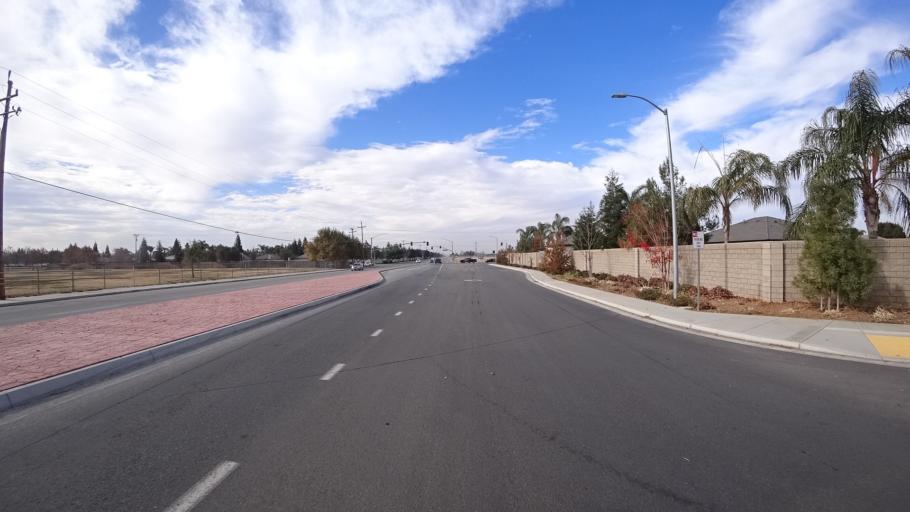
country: US
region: California
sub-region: Kern County
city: Greenacres
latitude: 35.4272
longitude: -119.1083
